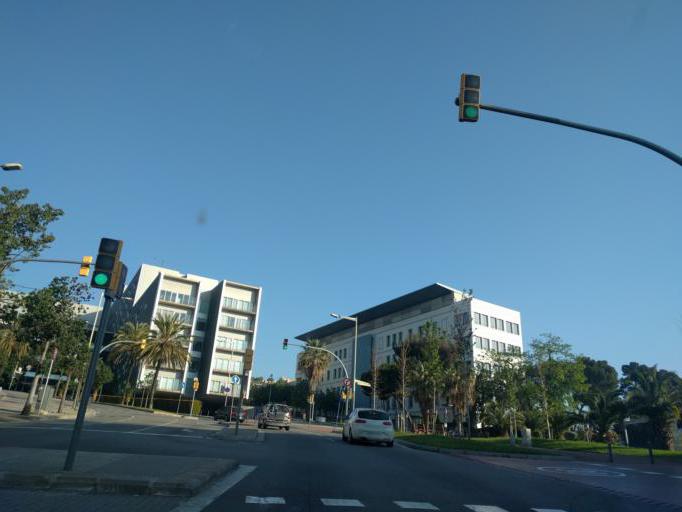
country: ES
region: Catalonia
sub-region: Provincia de Barcelona
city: Sarria-Sant Gervasi
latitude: 41.4148
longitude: 2.1399
